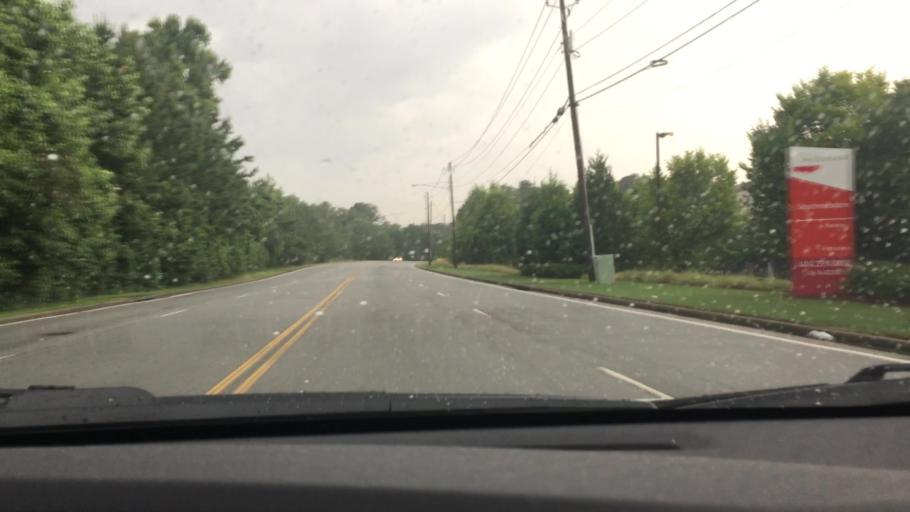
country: US
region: Georgia
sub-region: Fulton County
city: Union City
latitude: 33.6437
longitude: -84.5222
